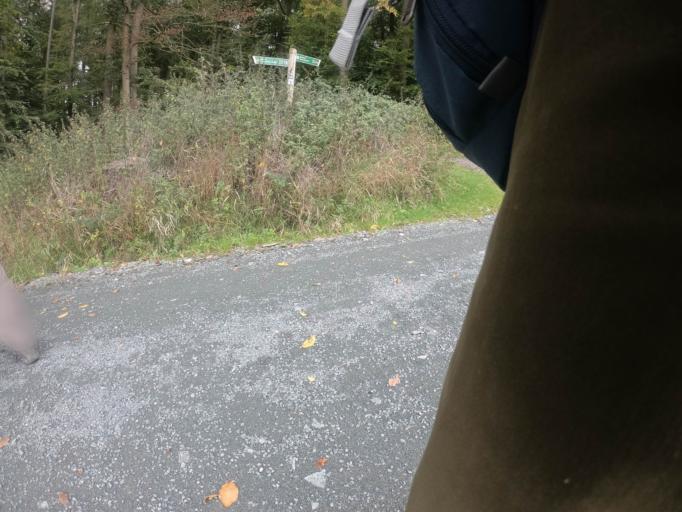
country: DE
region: Hesse
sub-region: Regierungsbezirk Darmstadt
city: Waldems
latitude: 50.2073
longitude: 8.3255
